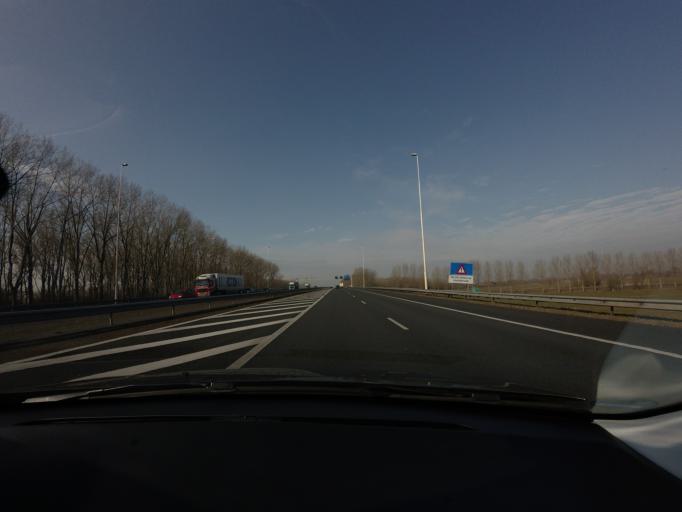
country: NL
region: Utrecht
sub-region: Gemeente Vianen
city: Vianen
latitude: 51.9552
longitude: 5.0595
